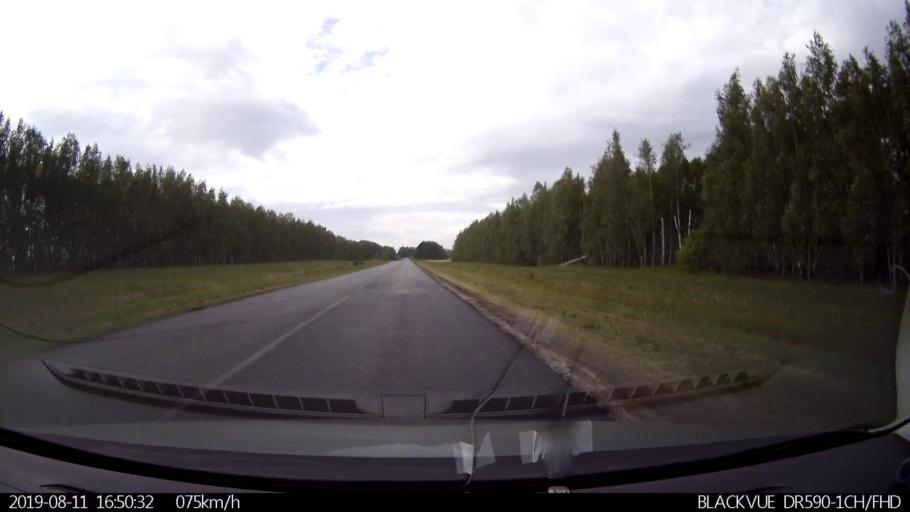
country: RU
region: Ulyanovsk
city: Mayna
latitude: 54.2296
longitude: 47.6863
